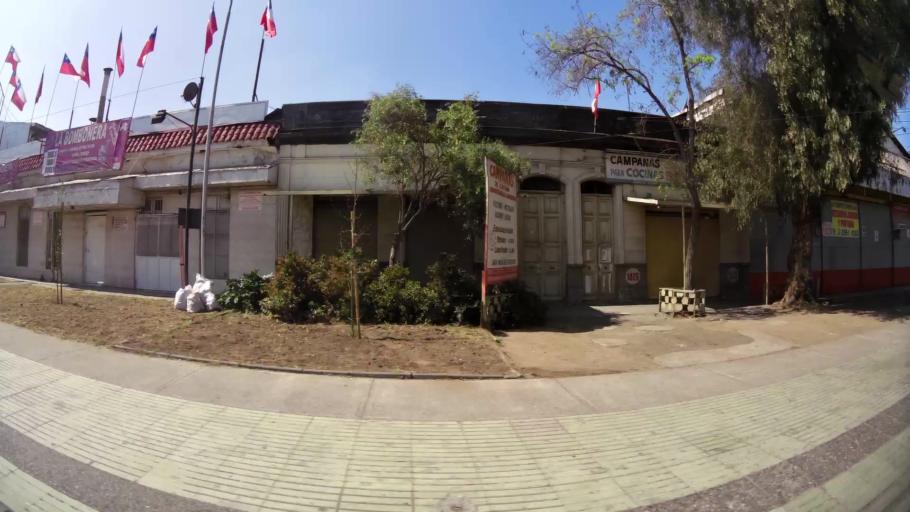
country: CL
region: Santiago Metropolitan
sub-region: Provincia de Santiago
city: Santiago
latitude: -33.4694
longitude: -70.6421
